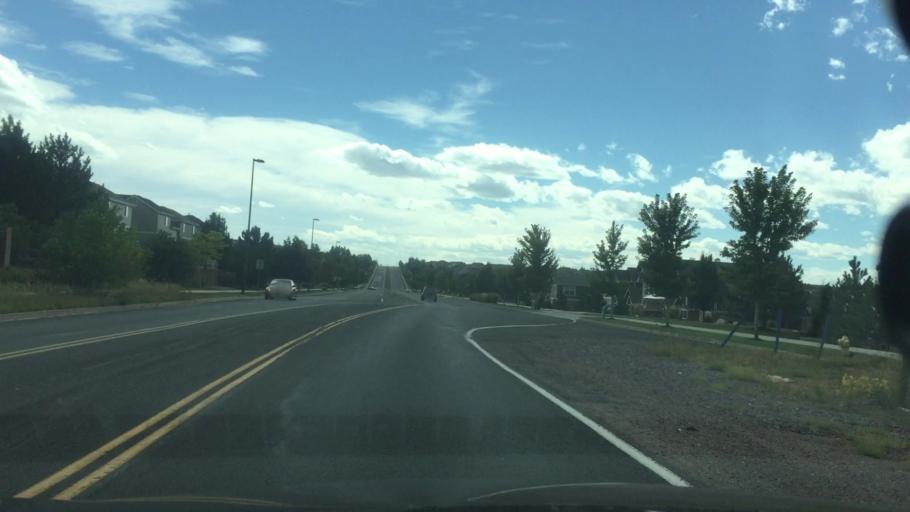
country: US
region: Colorado
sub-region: Arapahoe County
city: Dove Valley
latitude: 39.6501
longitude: -104.7350
